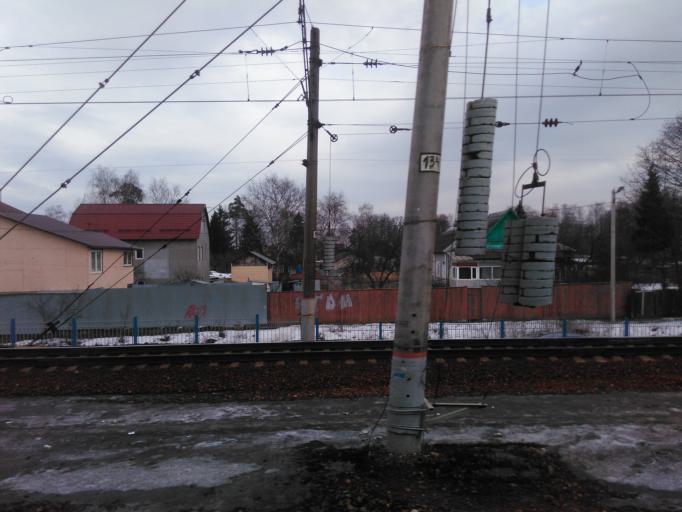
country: RU
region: Moskovskaya
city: Mamontovka
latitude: 55.9606
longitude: 37.8079
